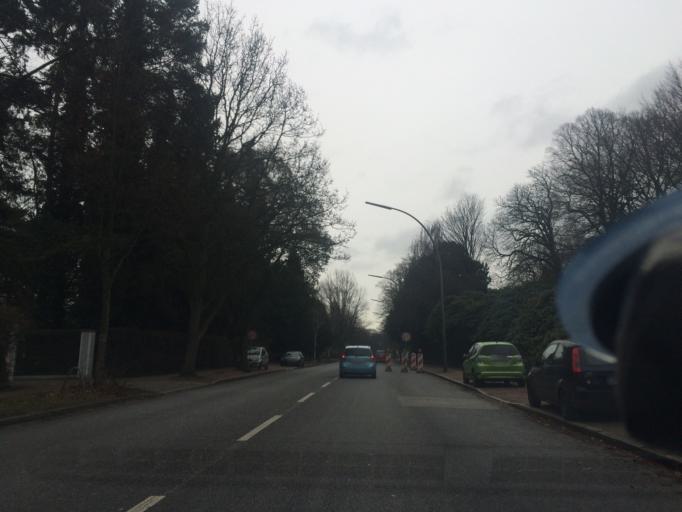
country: DE
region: Hamburg
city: Altona
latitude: 53.5465
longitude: 9.8937
